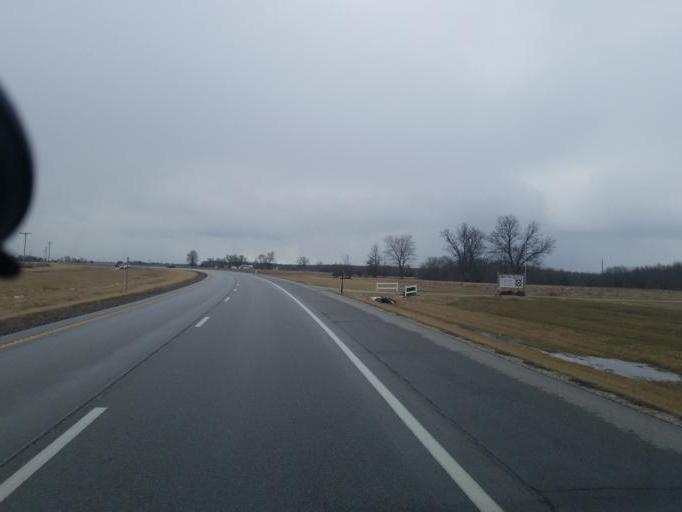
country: US
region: Missouri
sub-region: Macon County
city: Macon
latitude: 39.8462
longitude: -92.4813
